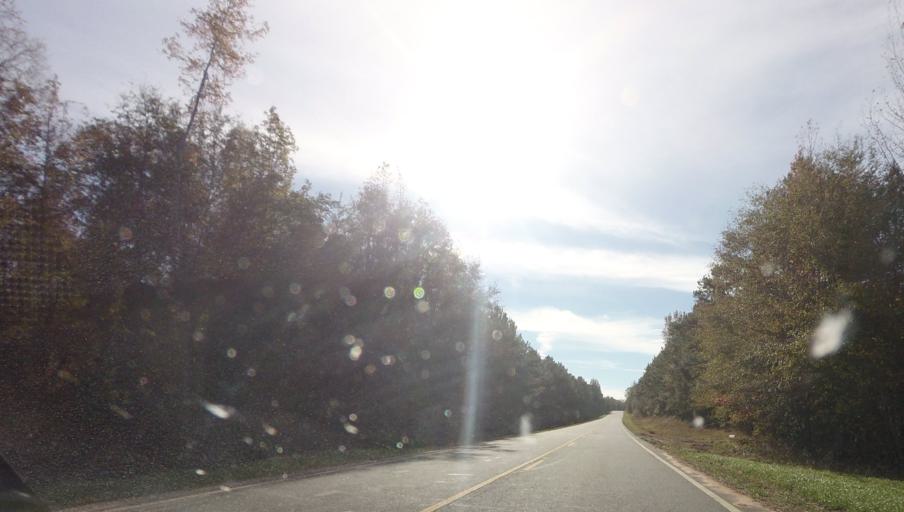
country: US
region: Georgia
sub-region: Talbot County
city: Talbotton
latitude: 32.7093
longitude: -84.3804
